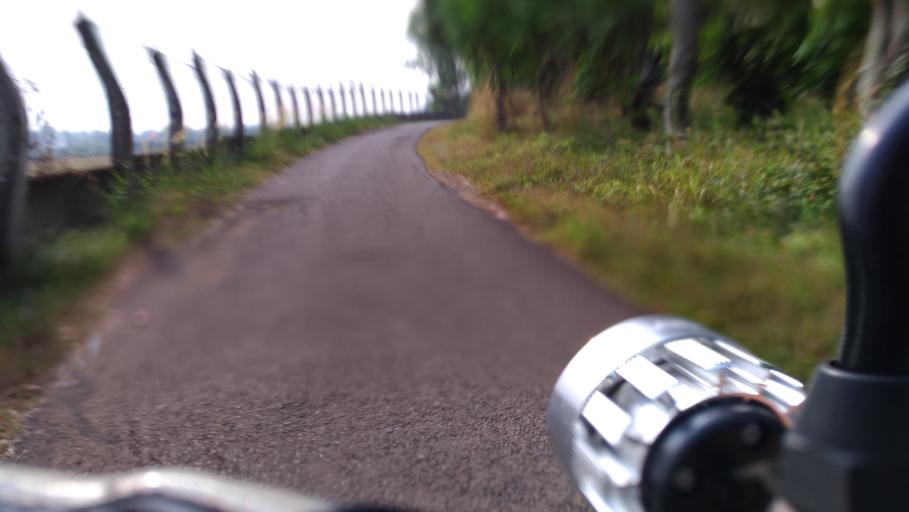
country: ID
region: West Java
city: Cileungsir
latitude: -6.3569
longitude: 106.8983
